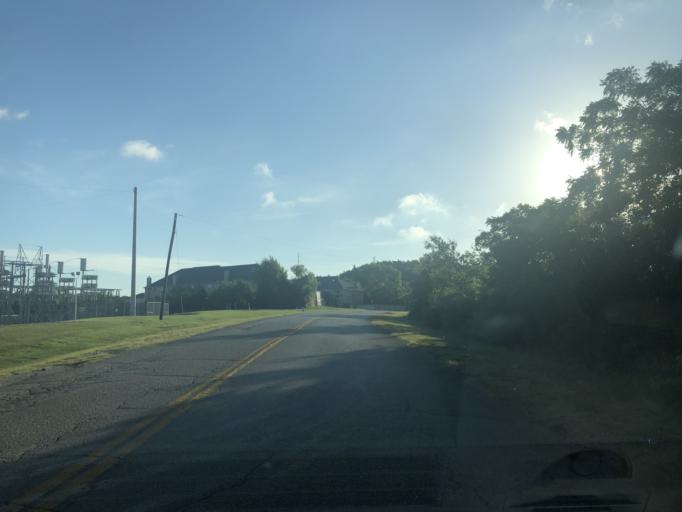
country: US
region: Texas
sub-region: Dallas County
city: Duncanville
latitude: 32.6647
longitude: -96.9602
